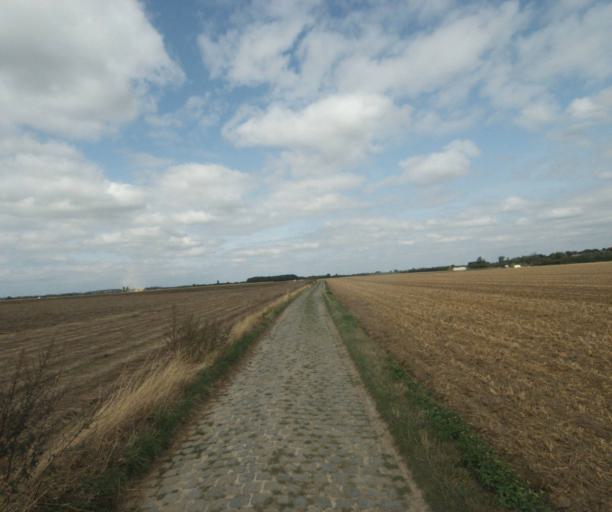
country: FR
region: Nord-Pas-de-Calais
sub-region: Departement du Nord
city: Baisieux
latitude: 50.5944
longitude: 3.2337
